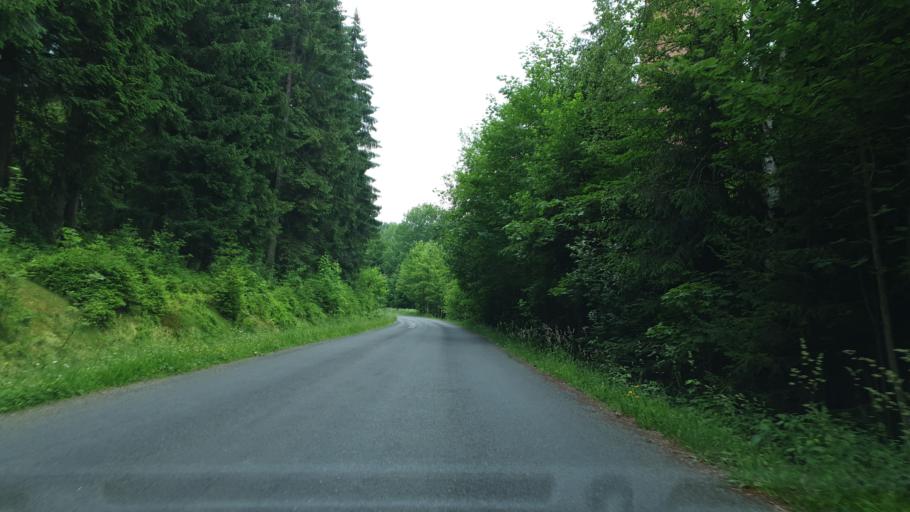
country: DE
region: Saxony
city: Tannenbergsthal
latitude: 50.4306
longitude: 12.4651
